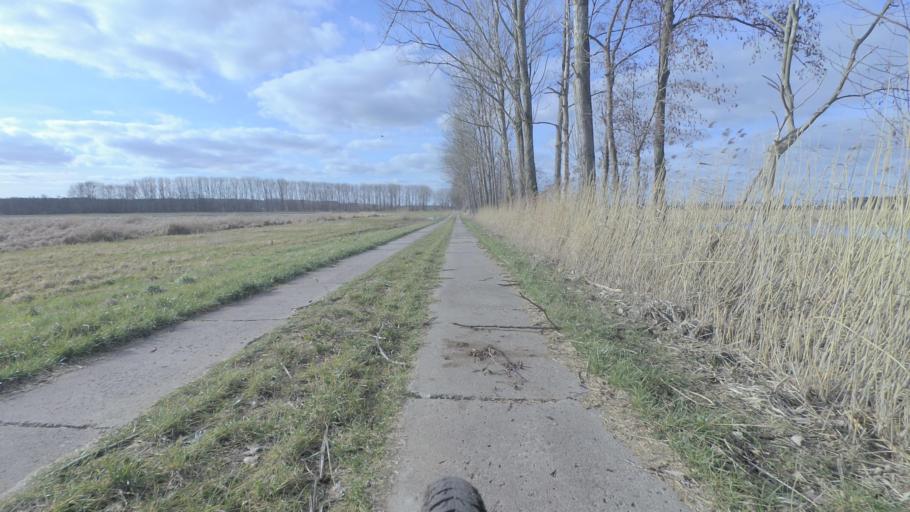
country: DE
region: Brandenburg
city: Trebbin
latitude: 52.2236
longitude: 13.2630
